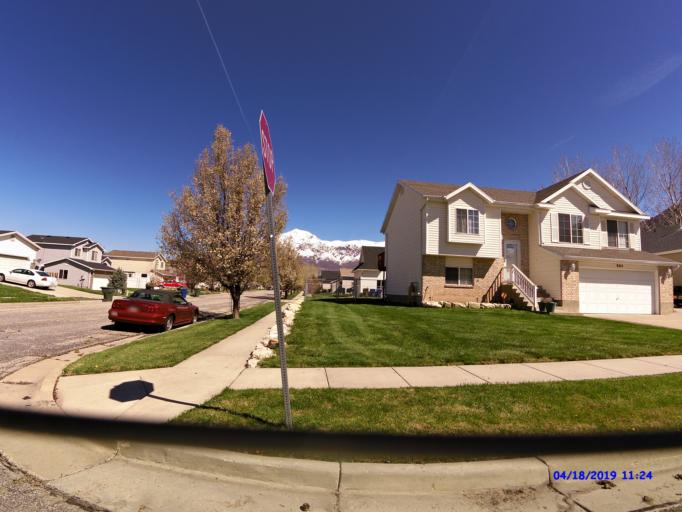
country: US
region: Utah
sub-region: Weber County
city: North Ogden
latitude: 41.2813
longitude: -111.9567
